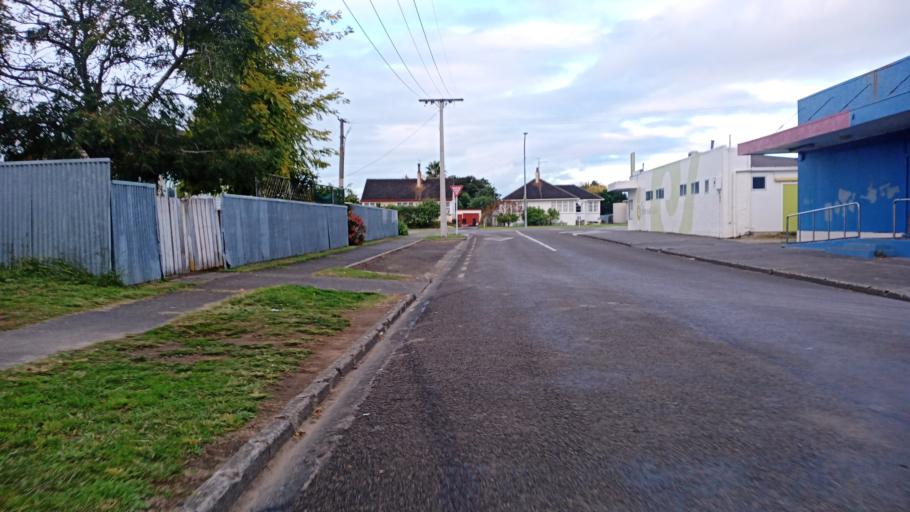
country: NZ
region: Gisborne
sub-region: Gisborne District
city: Gisborne
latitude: -38.6568
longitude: 177.9974
